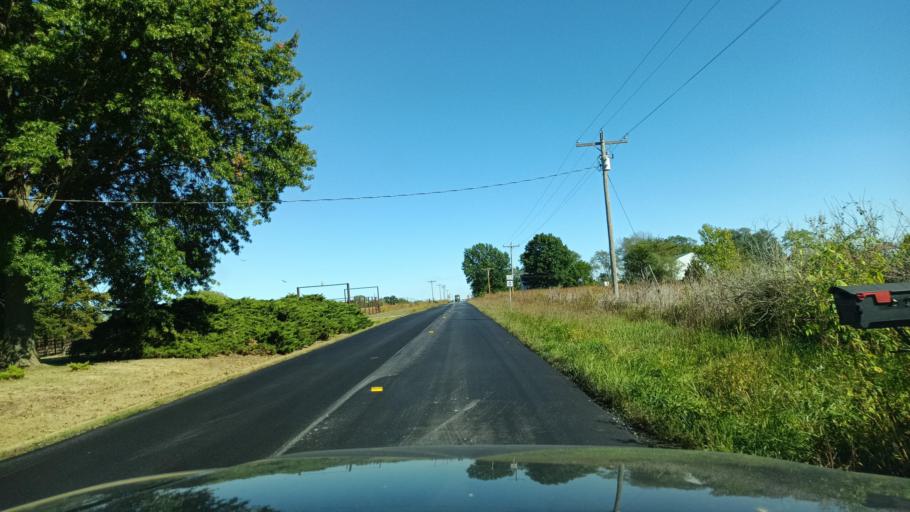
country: US
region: Missouri
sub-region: Macon County
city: La Plata
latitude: 39.9281
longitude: -92.5743
